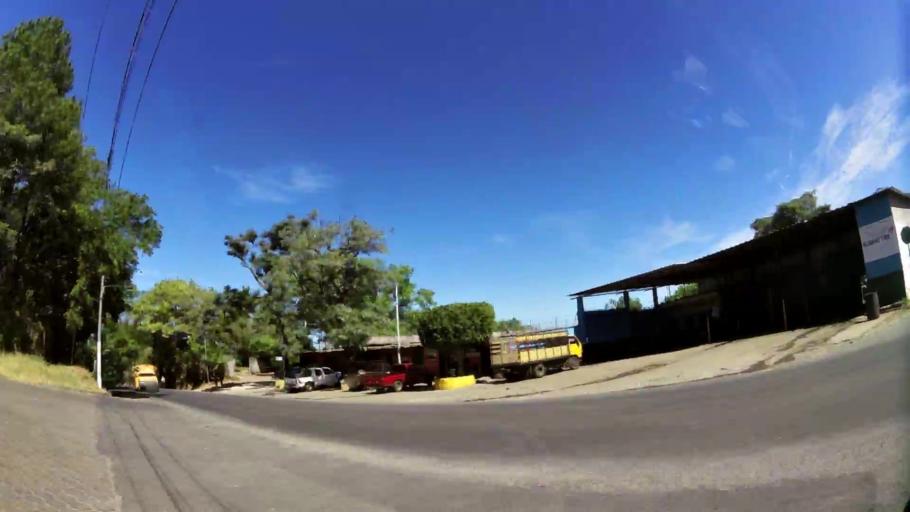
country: SV
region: Ahuachapan
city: Ahuachapan
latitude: 13.9223
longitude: -89.8418
